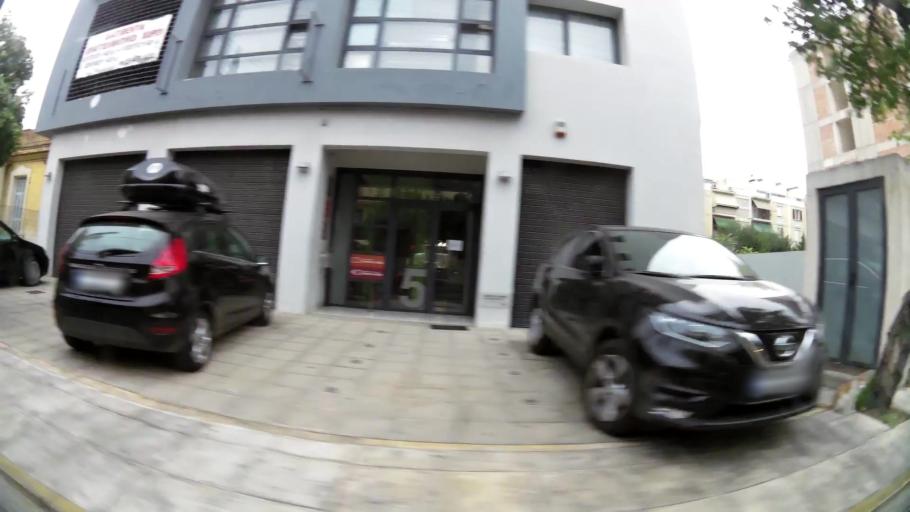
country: GR
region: Attica
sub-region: Nomos Piraios
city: Agios Ioannis Rentis
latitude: 37.9624
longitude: 23.6740
